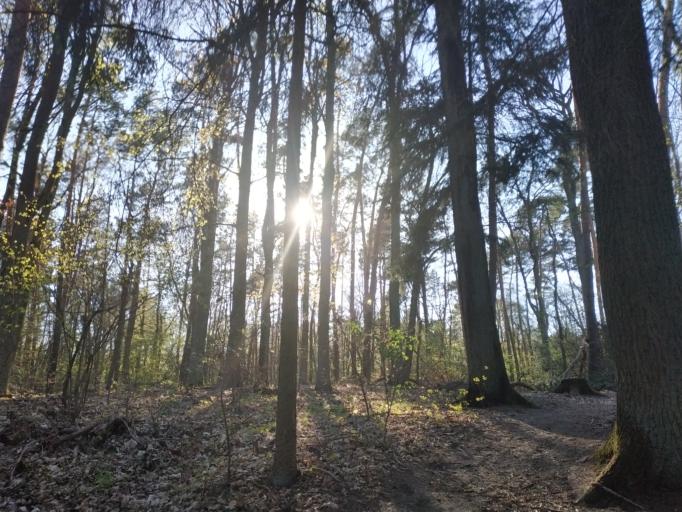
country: DE
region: Brandenburg
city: Strausberg
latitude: 52.5740
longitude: 13.8271
